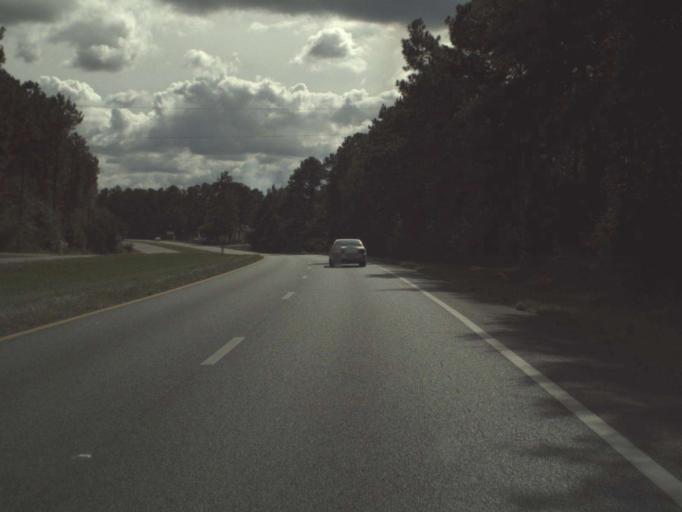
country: US
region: Florida
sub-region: Gadsden County
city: Havana
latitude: 30.6098
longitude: -84.4238
